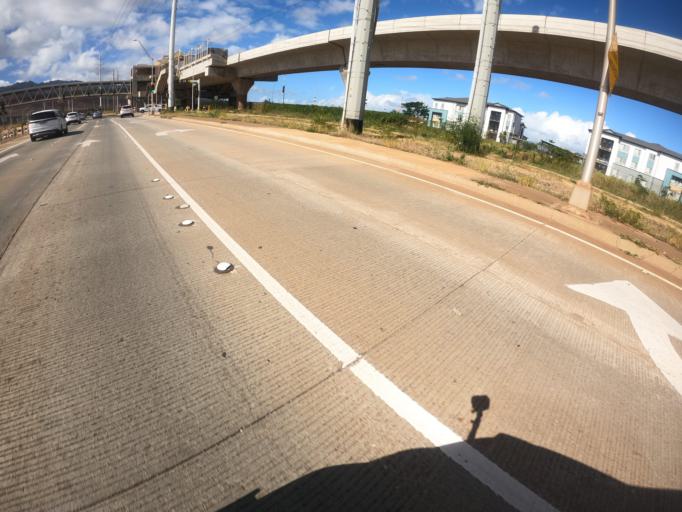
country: US
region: Hawaii
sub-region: Honolulu County
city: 'Ewa Villages
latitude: 21.3577
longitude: -158.0510
